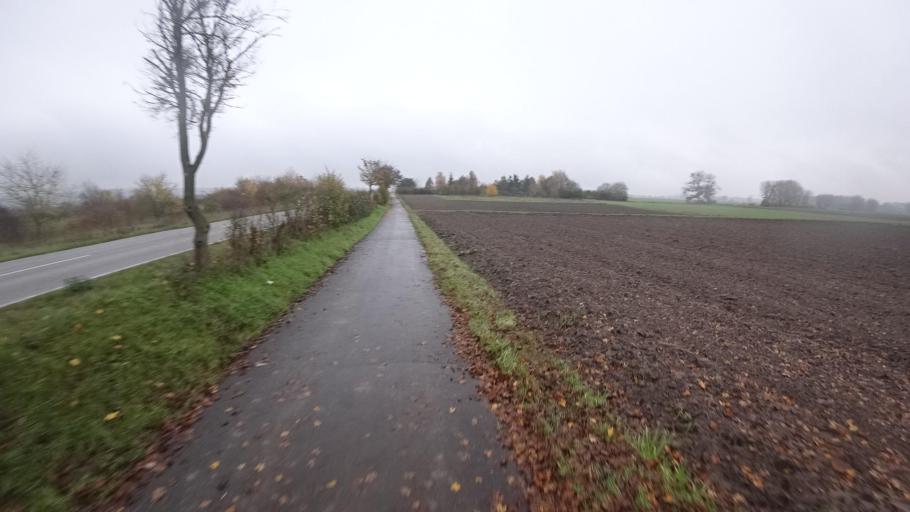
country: DE
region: Rheinland-Pfalz
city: Gimbsheim
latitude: 49.7864
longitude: 8.3676
